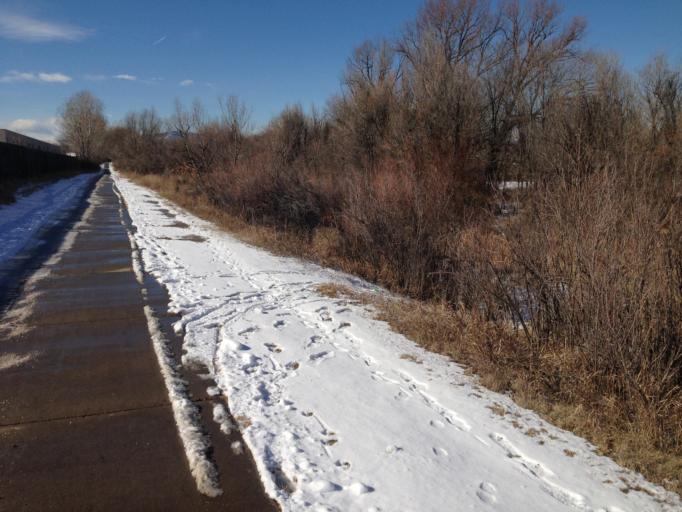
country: US
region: Colorado
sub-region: Adams County
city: Berkley
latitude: 39.7962
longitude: -105.0388
